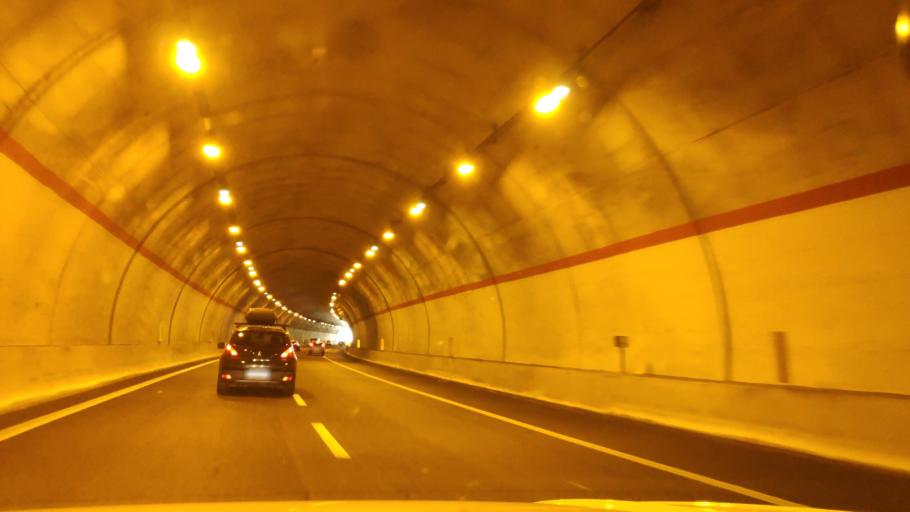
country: IT
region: Calabria
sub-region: Provincia di Cosenza
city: Morano Calabro
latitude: 39.8655
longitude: 16.0817
